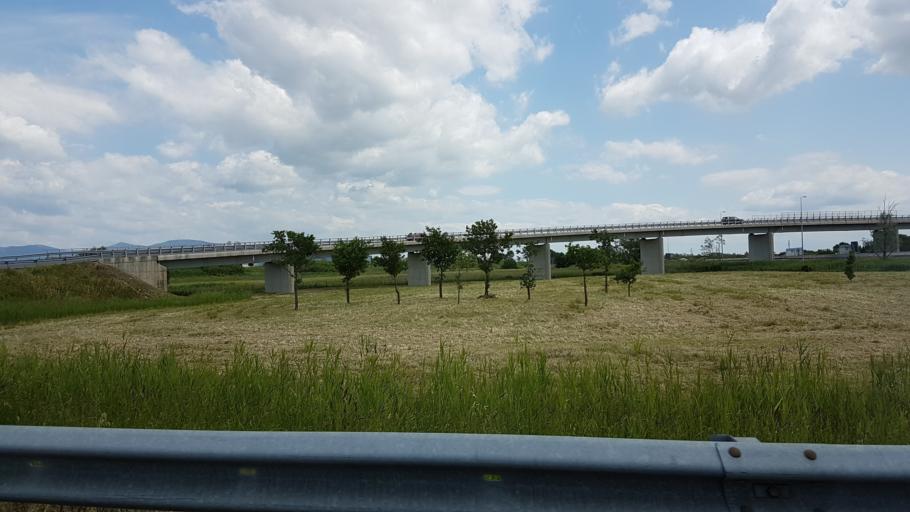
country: IT
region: Tuscany
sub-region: Provincia di Livorno
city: Vicarello
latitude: 43.6189
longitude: 10.4451
